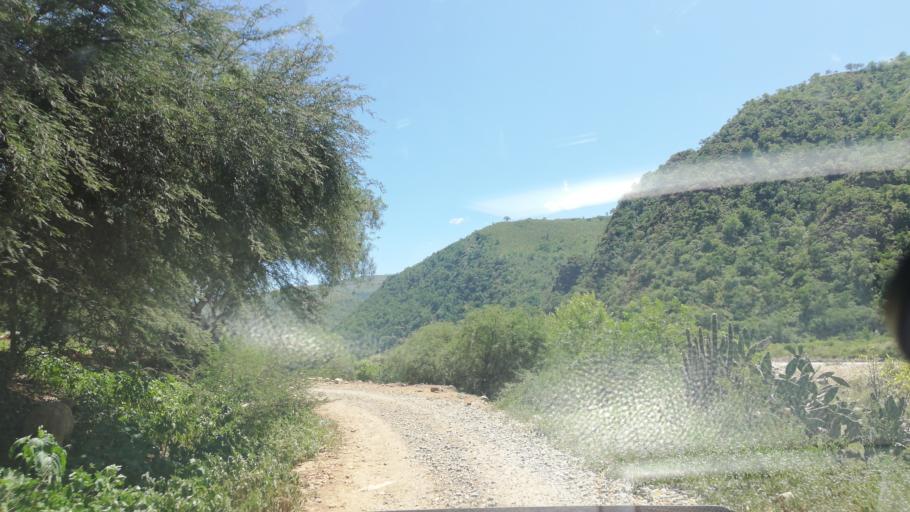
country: BO
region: Cochabamba
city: Mizque
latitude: -17.8262
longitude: -65.2932
